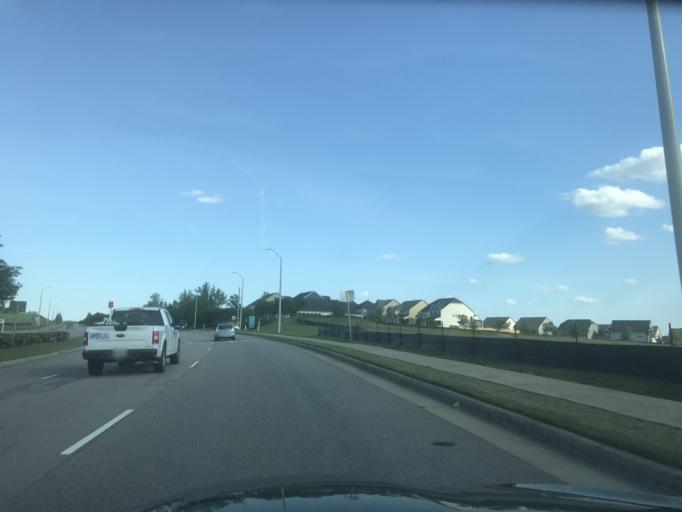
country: US
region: North Carolina
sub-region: Wake County
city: Knightdale
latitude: 35.7746
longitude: -78.4323
